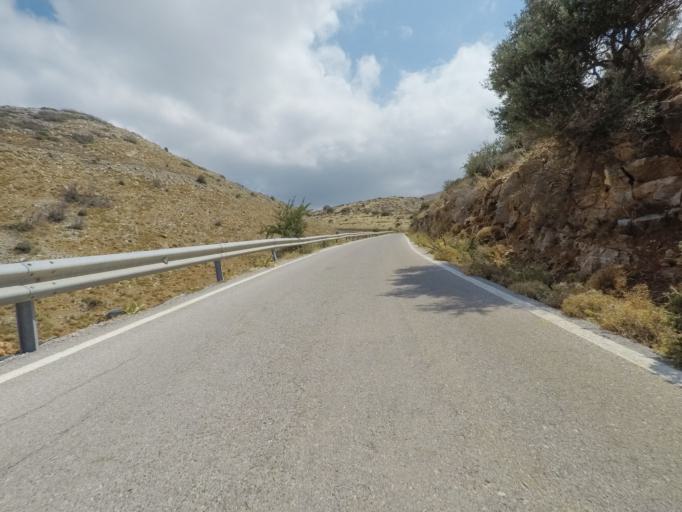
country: GR
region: Crete
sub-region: Nomos Lasithiou
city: Elounda
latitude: 35.3135
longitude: 25.6775
